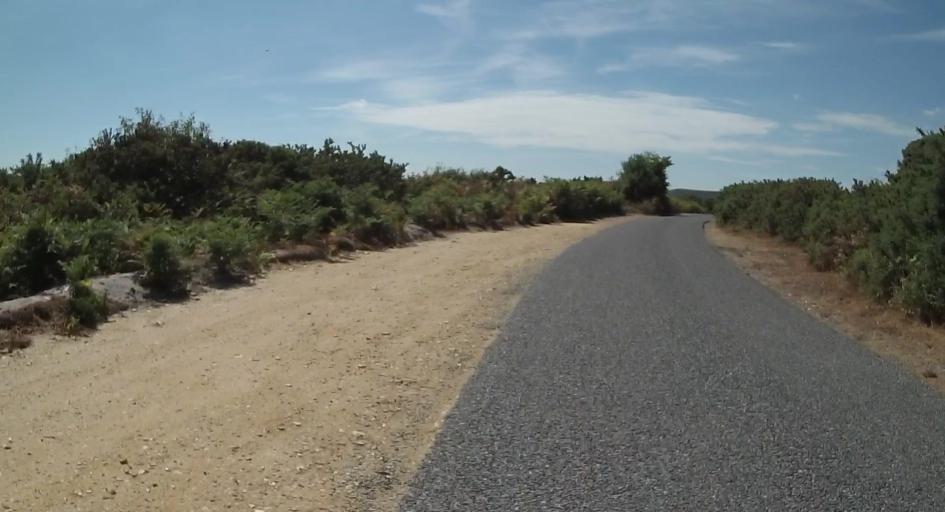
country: GB
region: England
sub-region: Dorset
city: Wareham
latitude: 50.6673
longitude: -2.0530
